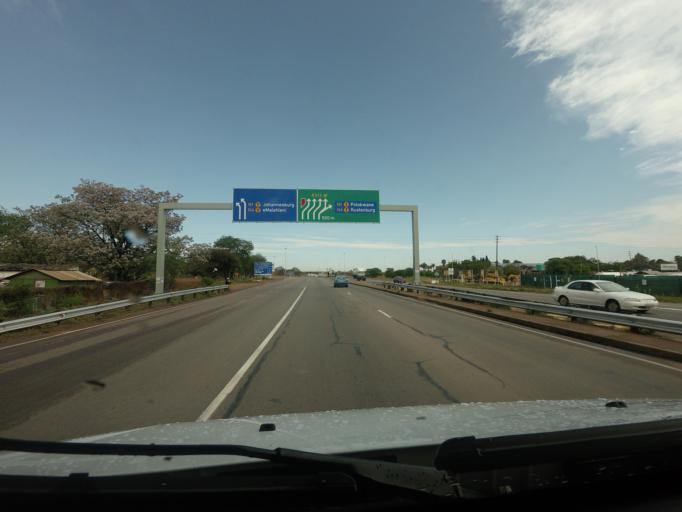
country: ZA
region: Gauteng
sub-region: City of Tshwane Metropolitan Municipality
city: Pretoria
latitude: -25.6851
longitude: 28.2844
